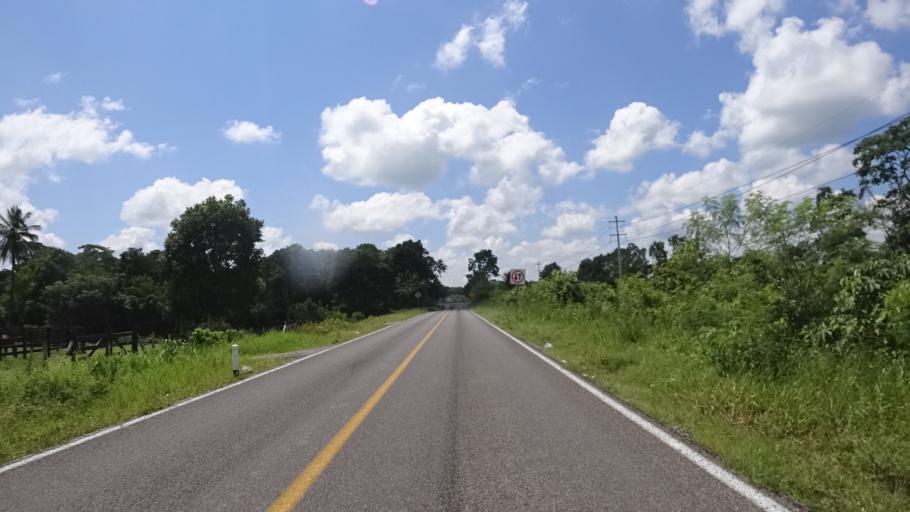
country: MX
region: Campeche
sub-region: Carmen
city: Licenciado Gustavo Diaz Ordaz (18 de Marzo)
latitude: 18.6325
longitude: -90.9827
